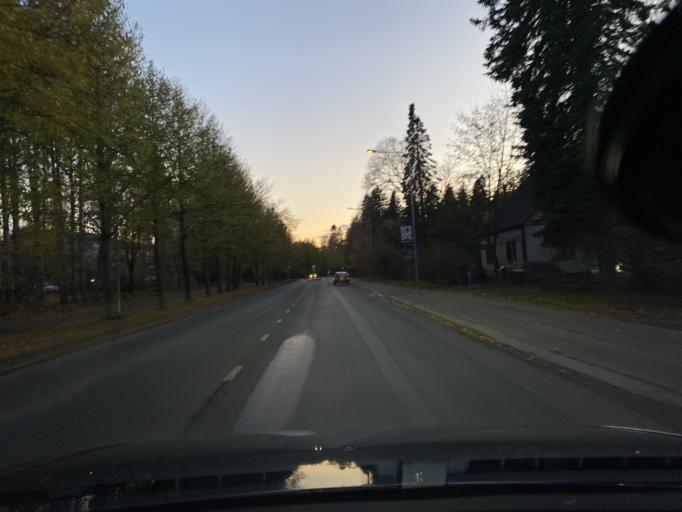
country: FI
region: Pirkanmaa
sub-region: Tampere
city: Tampere
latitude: 61.4723
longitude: 23.7568
